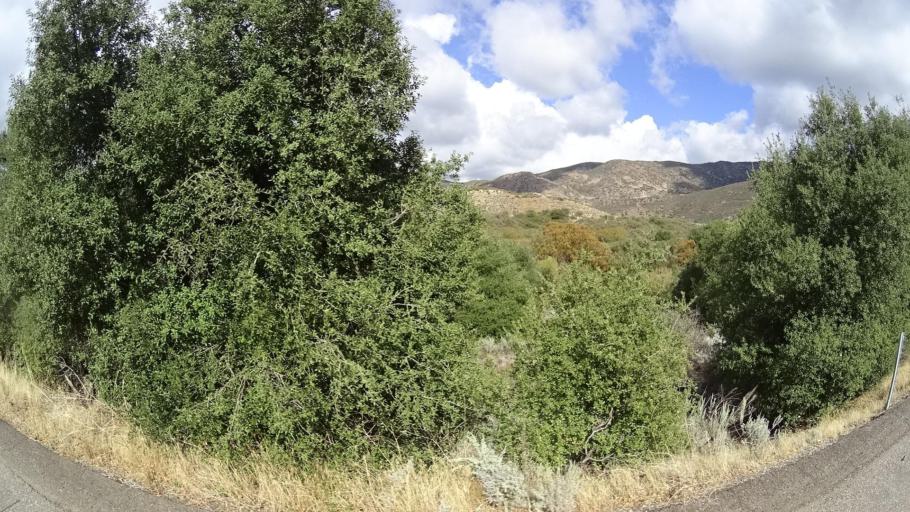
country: US
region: California
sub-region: San Diego County
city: Pine Valley
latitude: 32.8023
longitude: -116.5035
